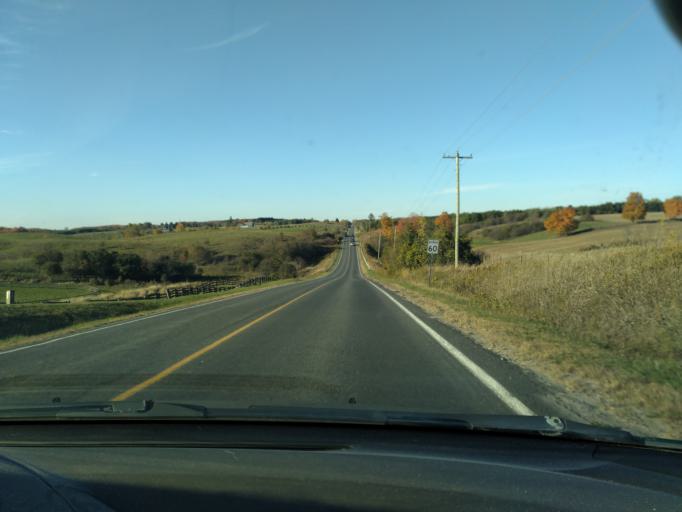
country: CA
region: Ontario
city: Bradford West Gwillimbury
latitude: 43.9338
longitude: -79.7113
